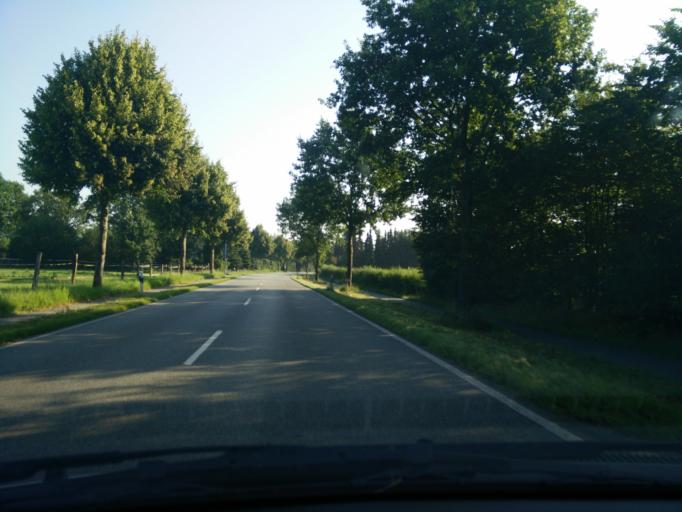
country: DE
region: Schleswig-Holstein
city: Prisdorf
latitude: 53.7094
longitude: 9.7423
